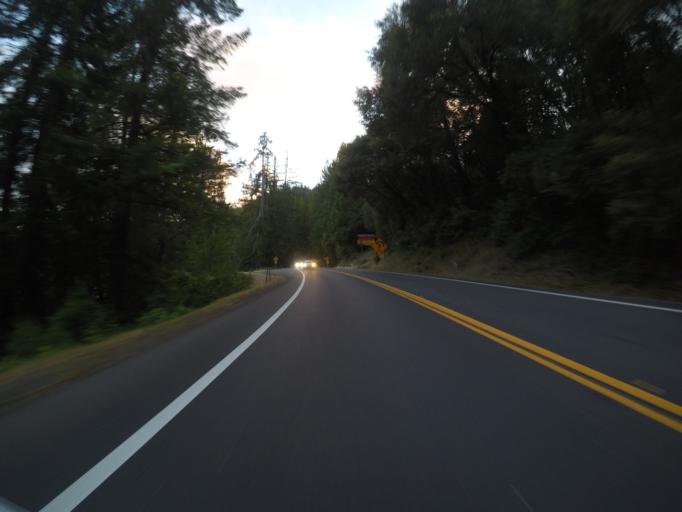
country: US
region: California
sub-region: Humboldt County
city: Redway
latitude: 40.0352
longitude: -123.7913
